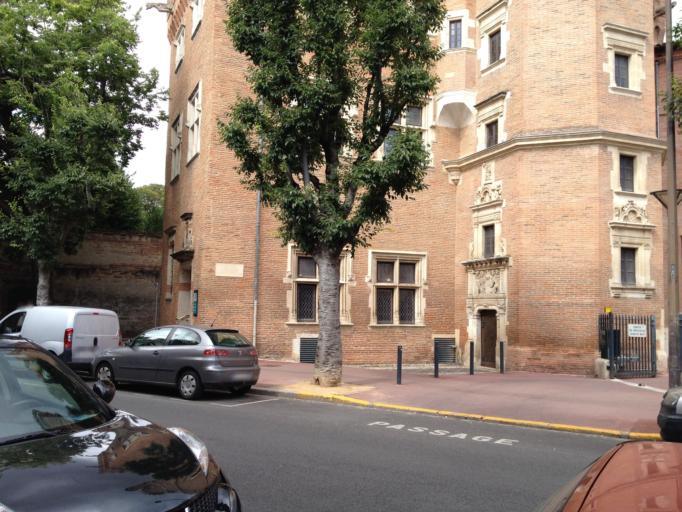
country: FR
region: Midi-Pyrenees
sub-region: Departement de la Haute-Garonne
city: Toulouse
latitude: 43.5971
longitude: 1.4463
